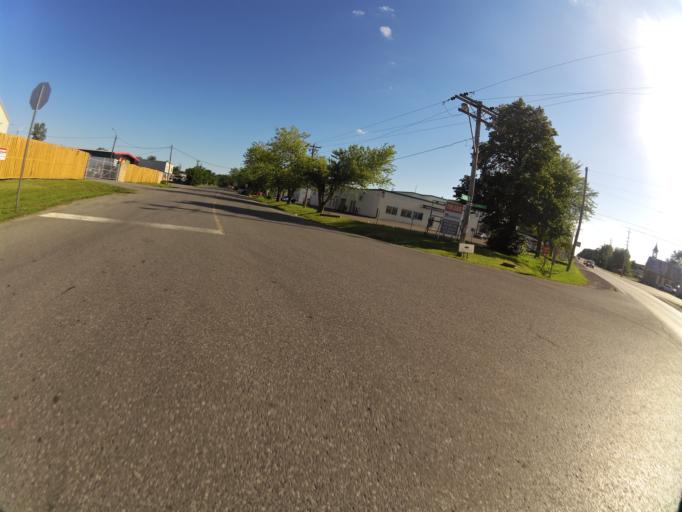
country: CA
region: Ontario
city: Ottawa
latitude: 45.3250
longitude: -75.7215
